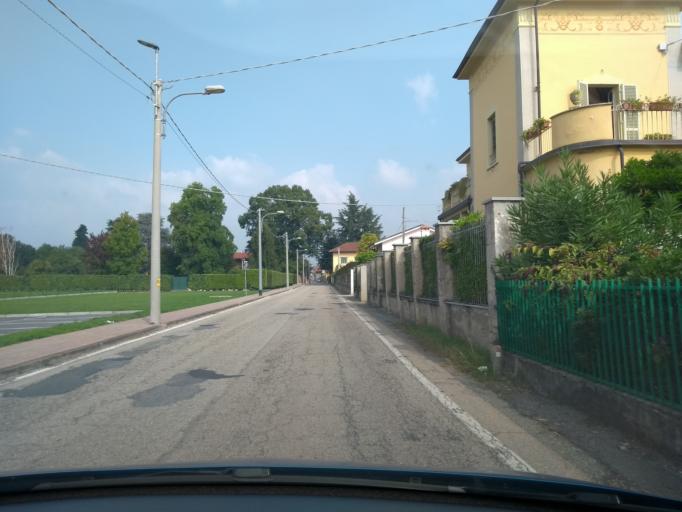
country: IT
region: Piedmont
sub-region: Provincia di Torino
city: Oglianico
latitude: 45.3382
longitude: 7.6918
